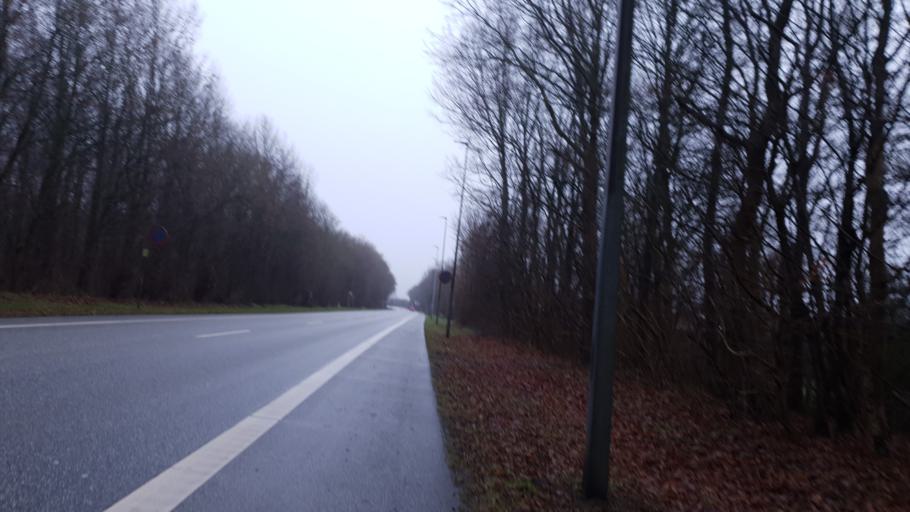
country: DK
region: Central Jutland
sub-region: Hedensted Kommune
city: Hedensted
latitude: 55.7852
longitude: 9.6988
